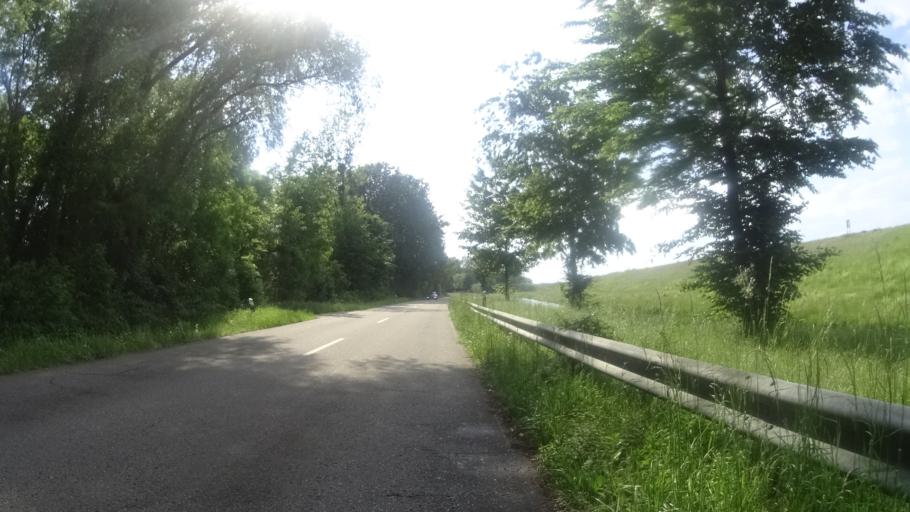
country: DE
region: Baden-Wuerttemberg
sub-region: Karlsruhe Region
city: Schwarzach
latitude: 48.7872
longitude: 8.0571
